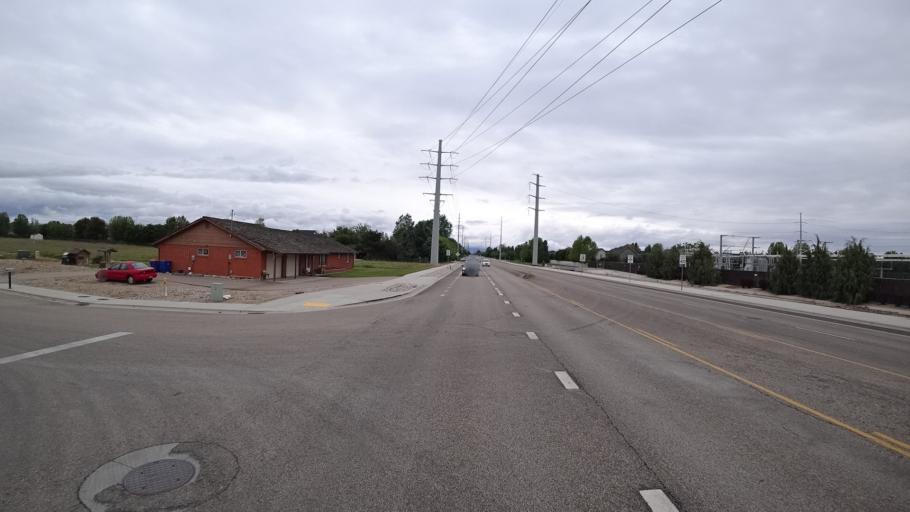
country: US
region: Idaho
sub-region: Ada County
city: Meridian
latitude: 43.6484
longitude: -116.3727
